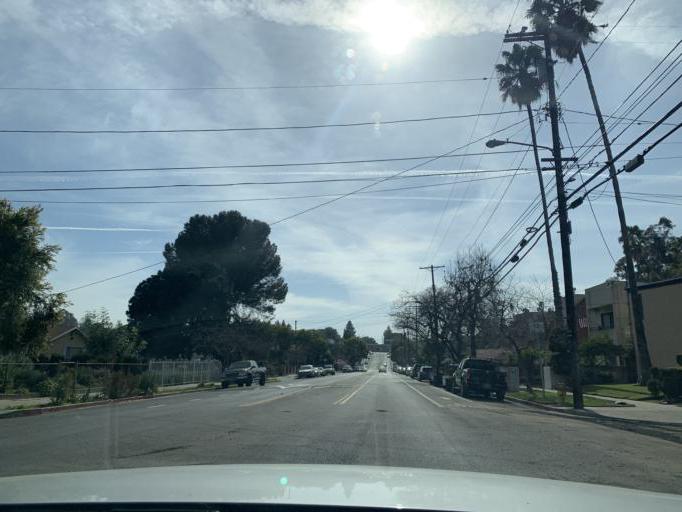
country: US
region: California
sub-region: Los Angeles County
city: South Pasadena
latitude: 34.1158
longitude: -118.1758
